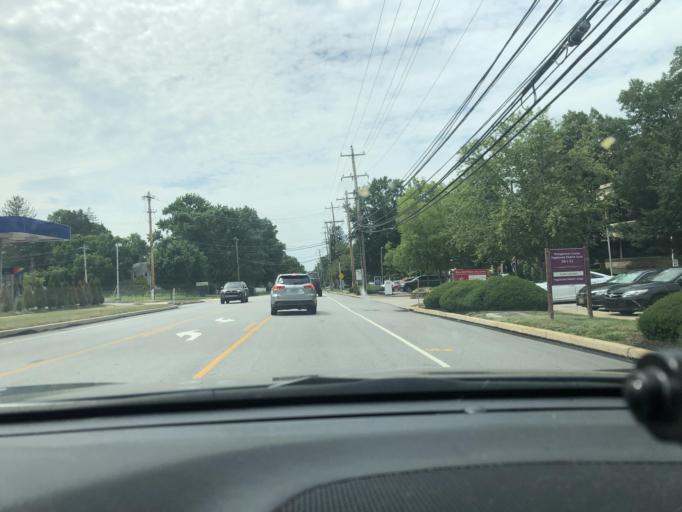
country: US
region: Pennsylvania
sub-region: Montgomery County
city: Blue Bell
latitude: 40.1533
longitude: -75.2676
